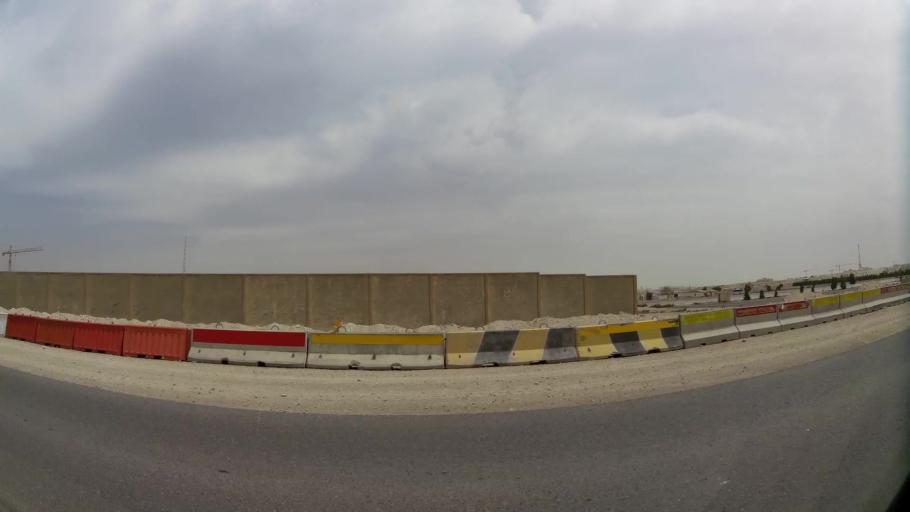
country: QA
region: Baladiyat ar Rayyan
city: Ar Rayyan
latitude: 25.2759
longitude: 51.4609
